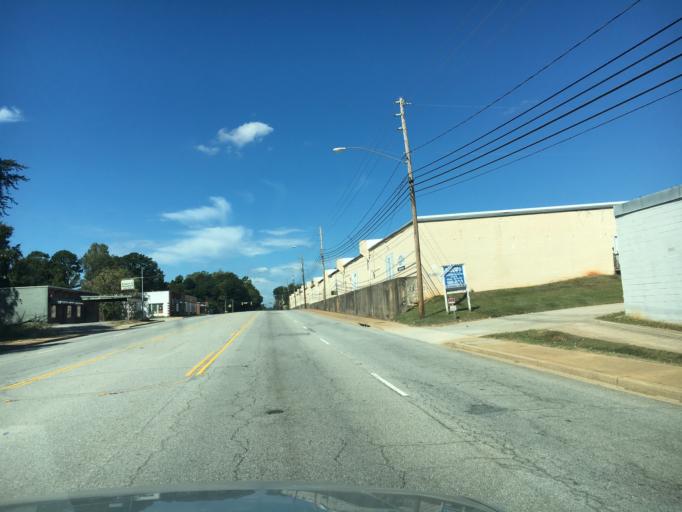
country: US
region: South Carolina
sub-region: Spartanburg County
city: Spartanburg
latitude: 34.9357
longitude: -81.9020
